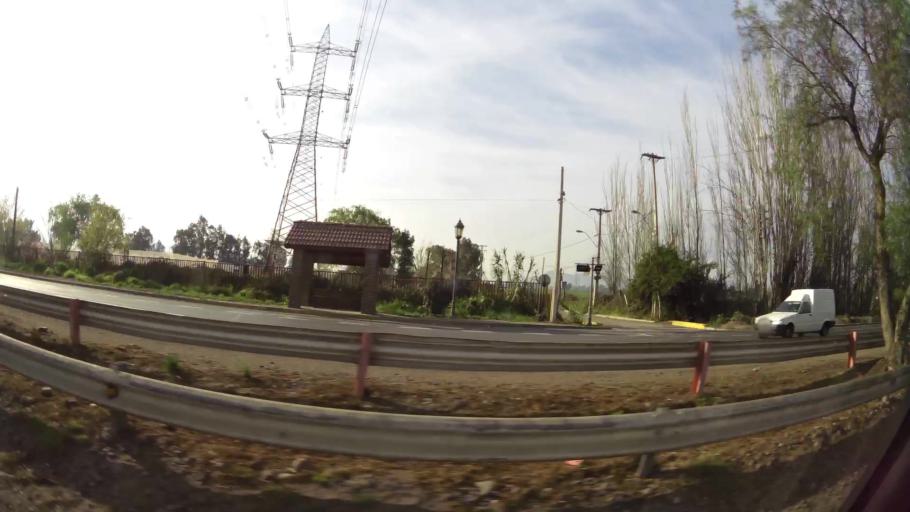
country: CL
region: Santiago Metropolitan
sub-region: Provincia de Talagante
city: Penaflor
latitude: -33.5857
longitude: -70.8348
